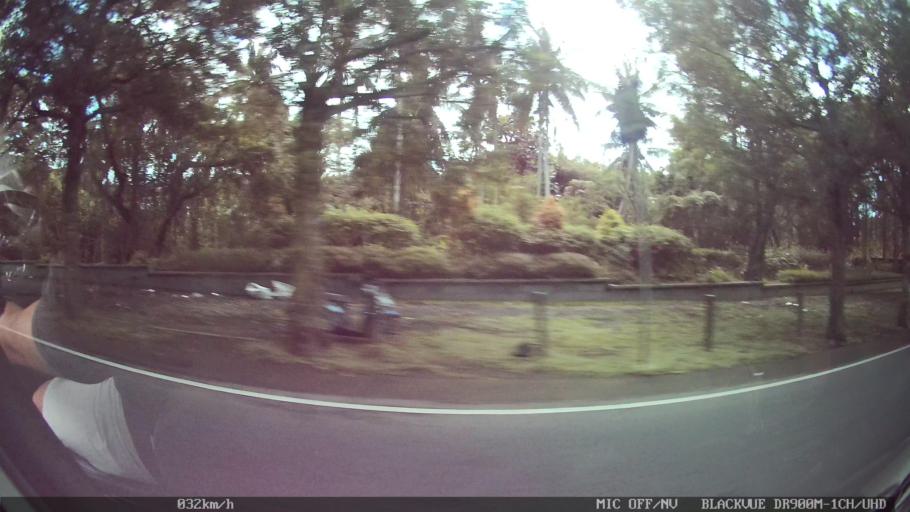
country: ID
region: Bali
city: Banjar Sedang
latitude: -8.5661
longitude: 115.2919
